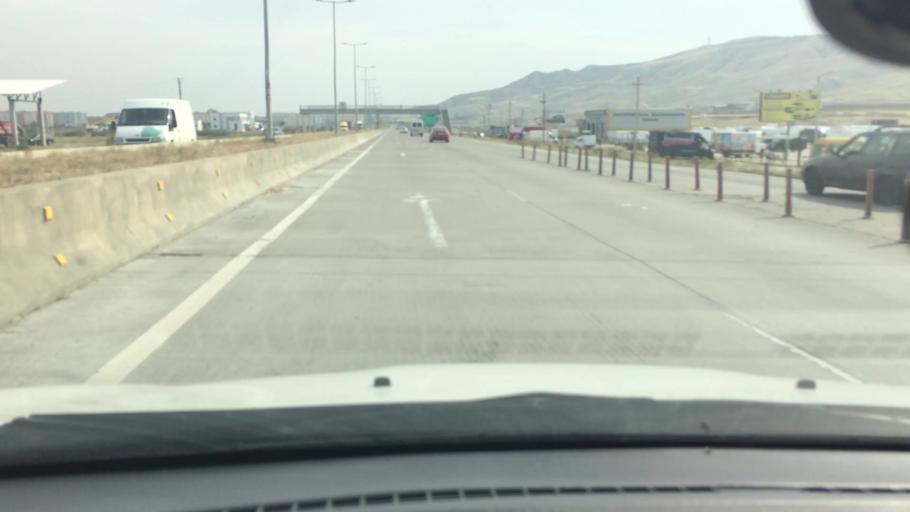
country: GE
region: Kvemo Kartli
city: Rust'avi
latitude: 41.5841
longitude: 44.9512
